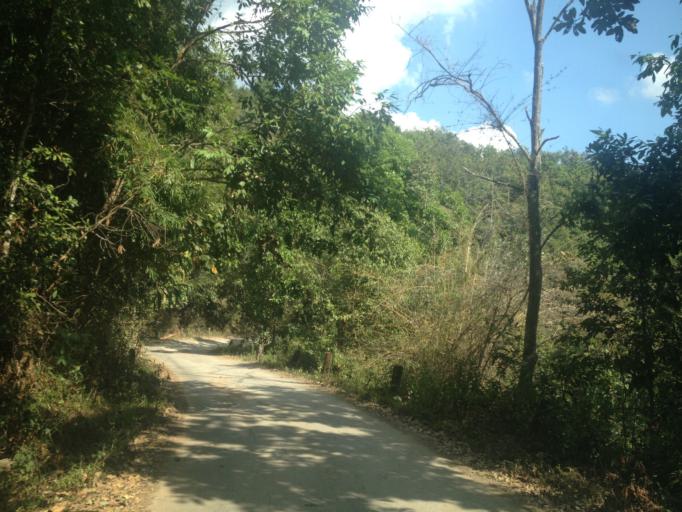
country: TH
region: Mae Hong Son
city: Ban Huai I Huak
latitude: 18.1141
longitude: 98.1538
